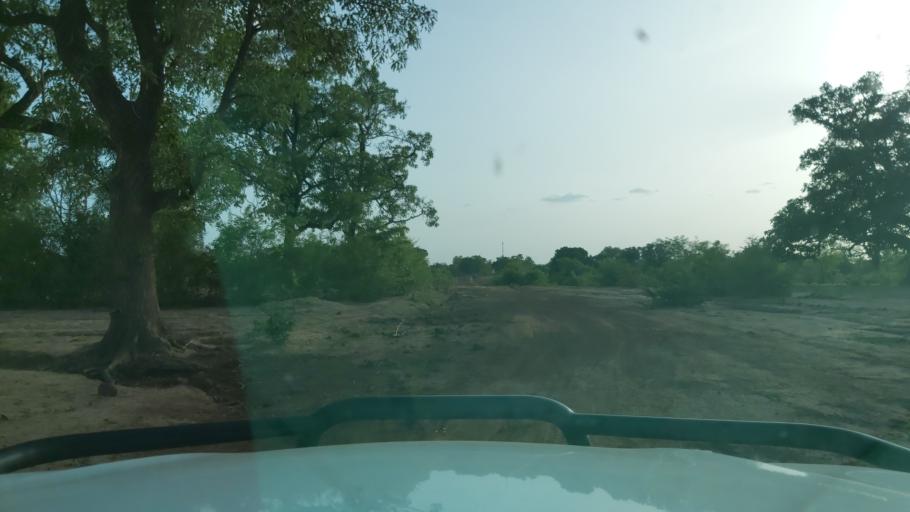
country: ML
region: Koulikoro
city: Kolokani
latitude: 13.2057
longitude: -7.9182
